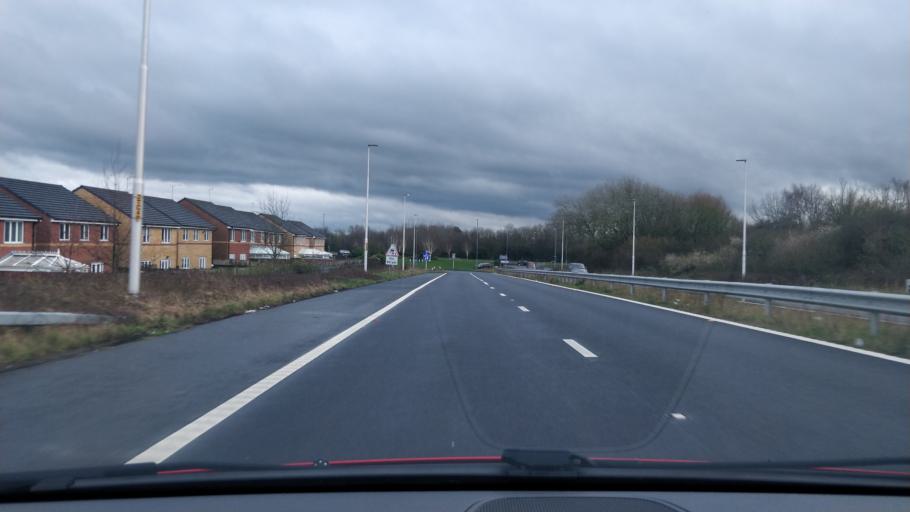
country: GB
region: England
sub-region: Knowsley
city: Knowsley
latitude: 53.4310
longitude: -2.8561
